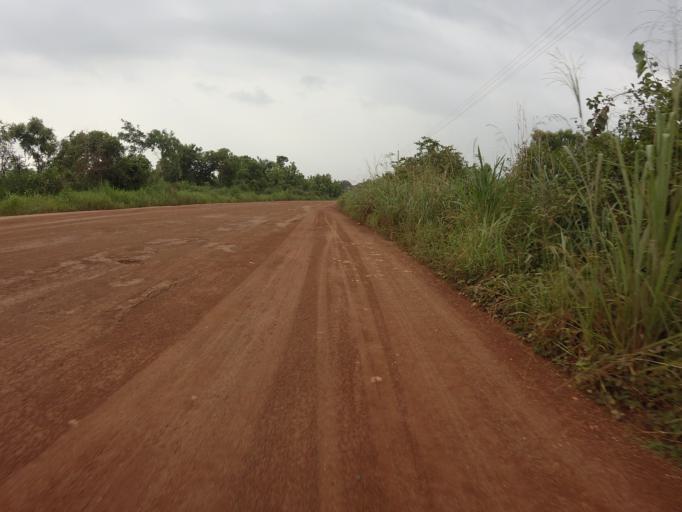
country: GH
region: Volta
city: Kpandu
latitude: 7.0112
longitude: 0.4286
